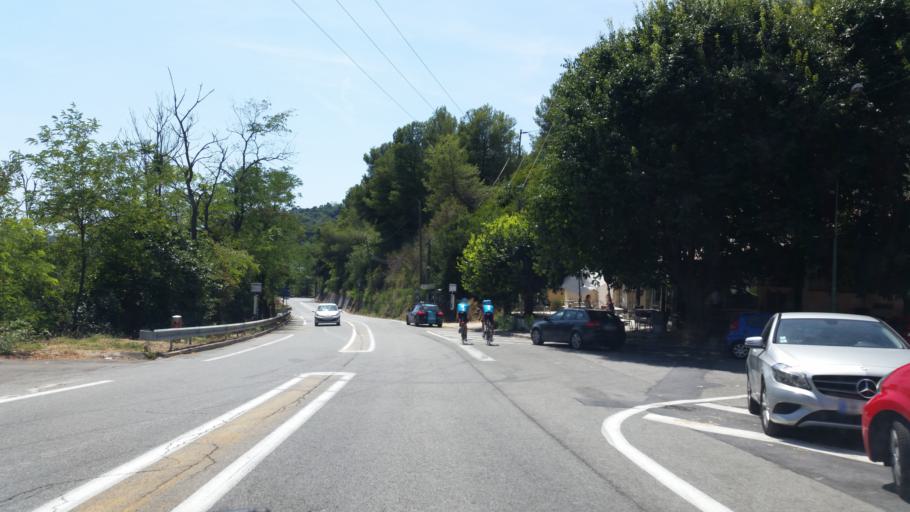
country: FR
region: Provence-Alpes-Cote d'Azur
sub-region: Departement des Alpes-Maritimes
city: Sainte-Agnes
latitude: 43.8061
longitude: 7.4857
